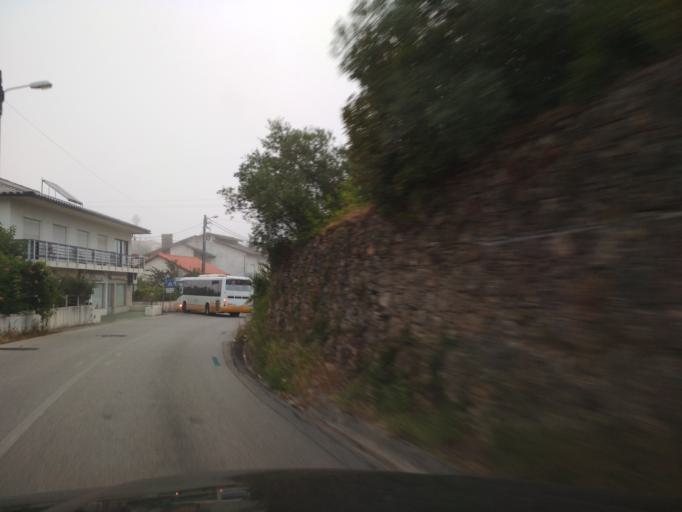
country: PT
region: Coimbra
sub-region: Coimbra
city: Coimbra
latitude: 40.1854
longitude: -8.4421
